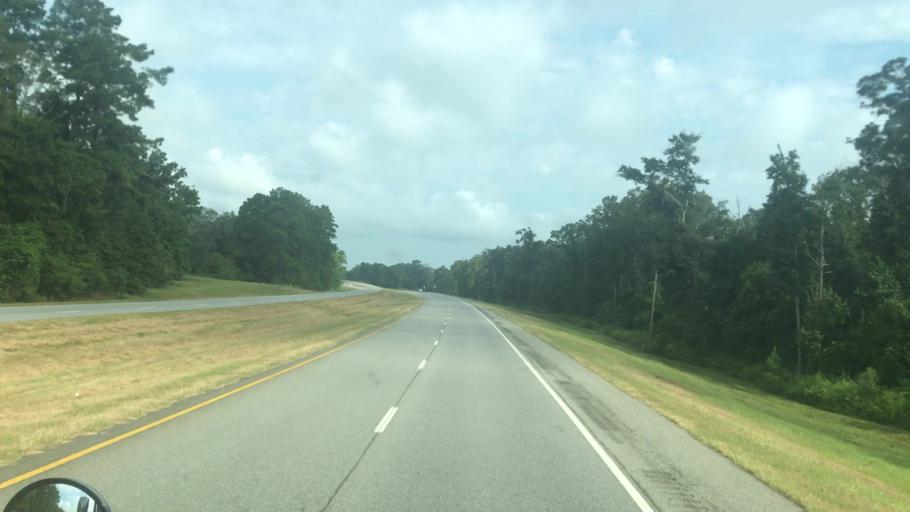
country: US
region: Georgia
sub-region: Miller County
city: Colquitt
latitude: 31.2433
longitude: -84.7901
